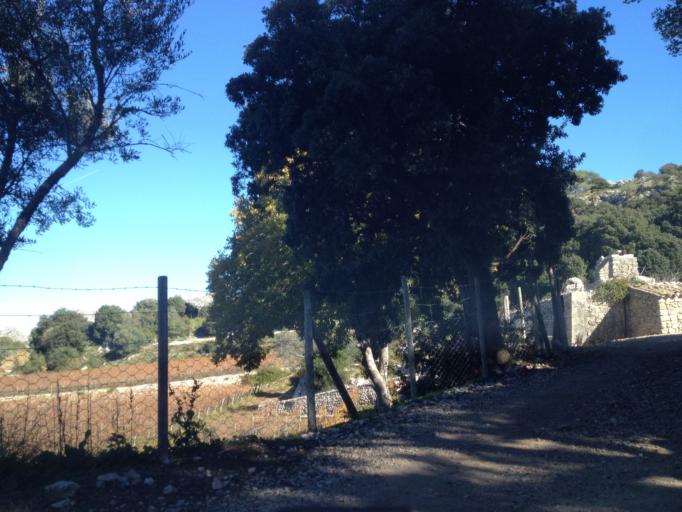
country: ES
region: Balearic Islands
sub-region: Illes Balears
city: Escorca
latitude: 39.8701
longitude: 2.9240
